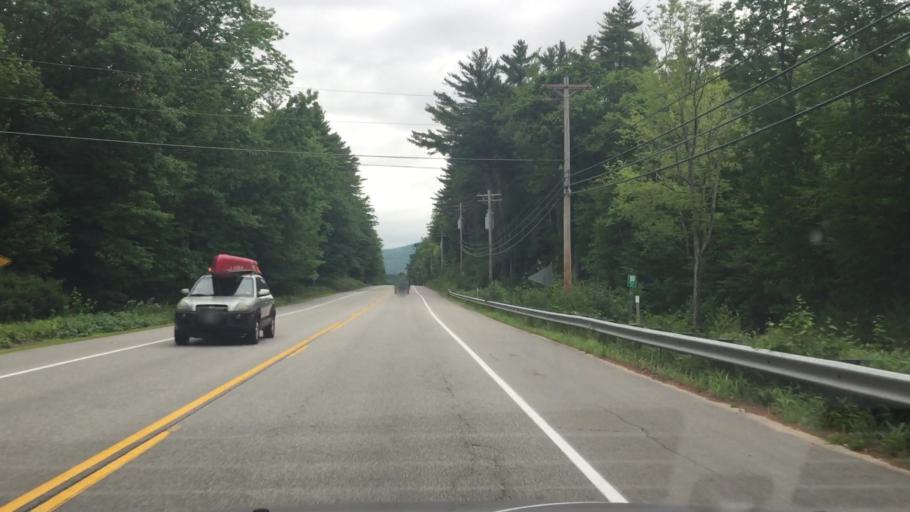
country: US
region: New Hampshire
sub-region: Carroll County
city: Center Harbor
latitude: 43.6917
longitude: -71.4587
